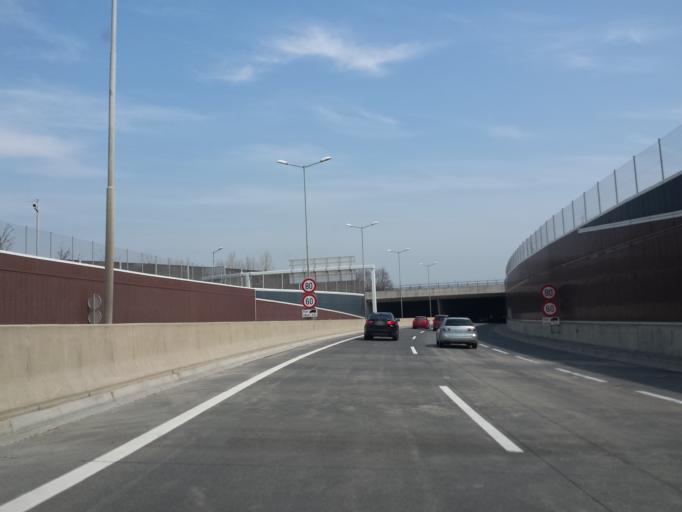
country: AT
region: Lower Austria
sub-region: Politischer Bezirk Wien-Umgebung
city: Gerasdorf bei Wien
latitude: 48.2679
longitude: 16.4792
